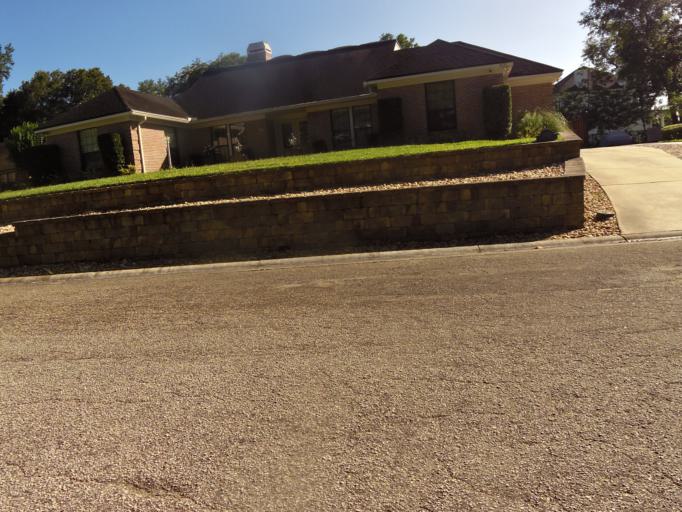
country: US
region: Florida
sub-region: Duval County
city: Jacksonville
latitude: 30.3145
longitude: -81.6187
